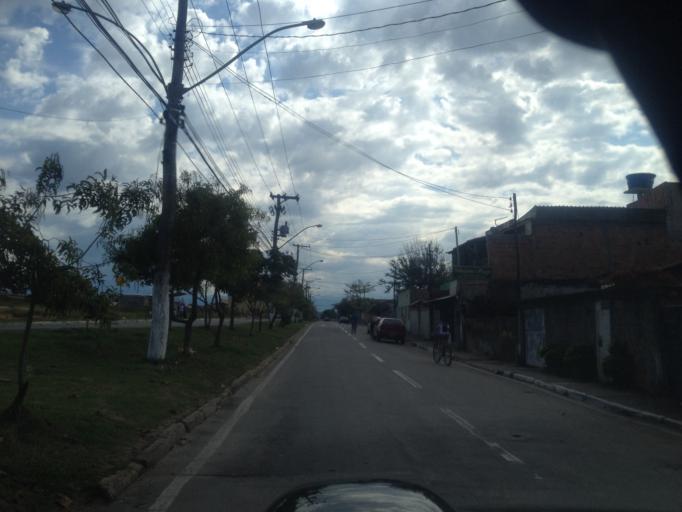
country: BR
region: Rio de Janeiro
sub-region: Porto Real
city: Porto Real
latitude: -22.4163
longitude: -44.3059
